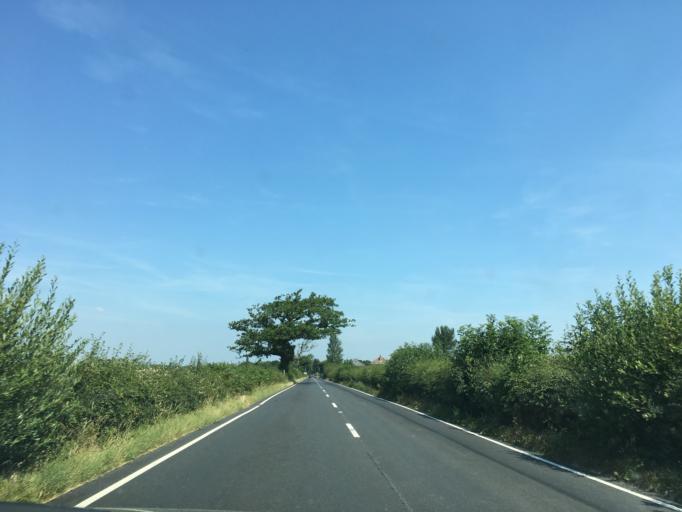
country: GB
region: England
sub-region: Isle of Wight
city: Newport
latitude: 50.7110
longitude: -1.2456
